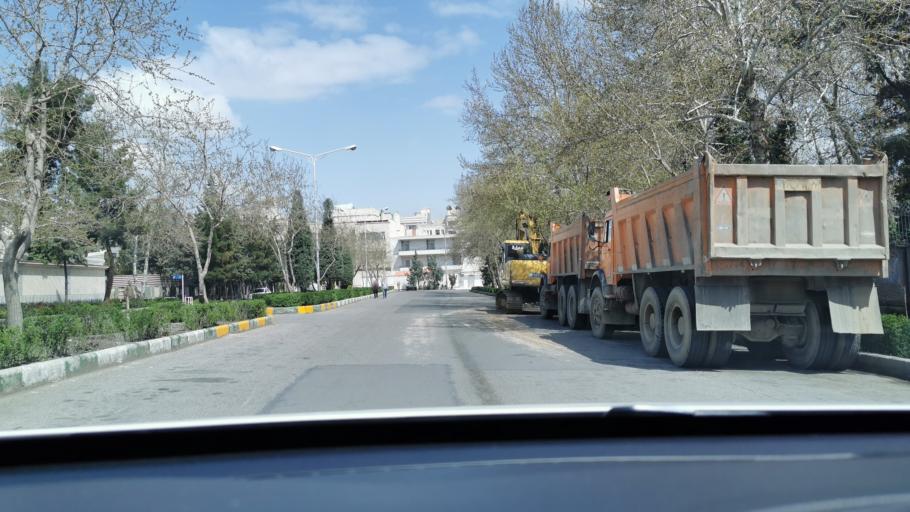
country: IR
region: Razavi Khorasan
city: Mashhad
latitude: 36.3196
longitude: 59.5307
